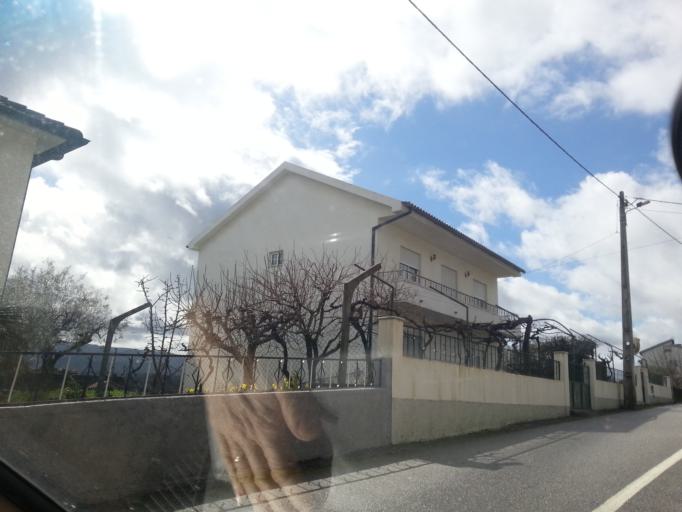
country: PT
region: Guarda
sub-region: Fornos de Algodres
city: Fornos de Algodres
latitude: 40.6090
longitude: -7.4910
